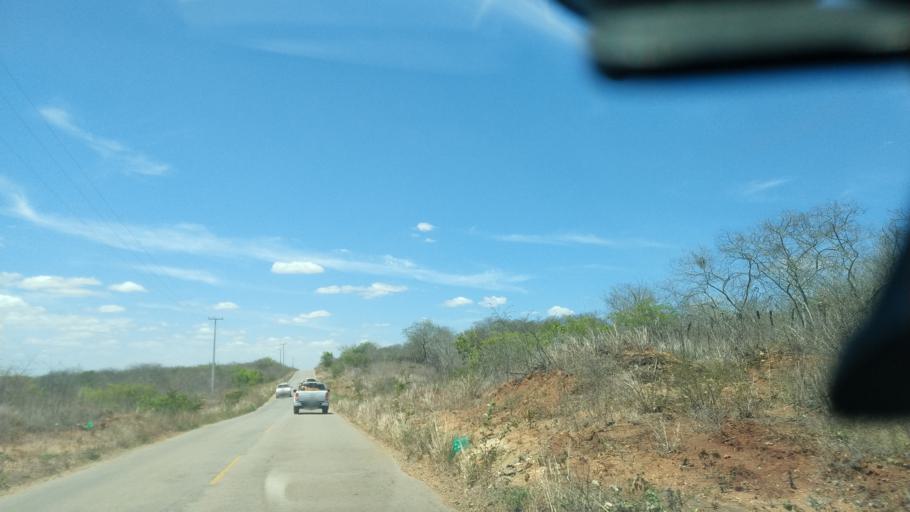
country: BR
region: Rio Grande do Norte
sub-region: Sao Paulo Do Potengi
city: Sao Paulo do Potengi
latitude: -5.9057
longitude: -35.6074
